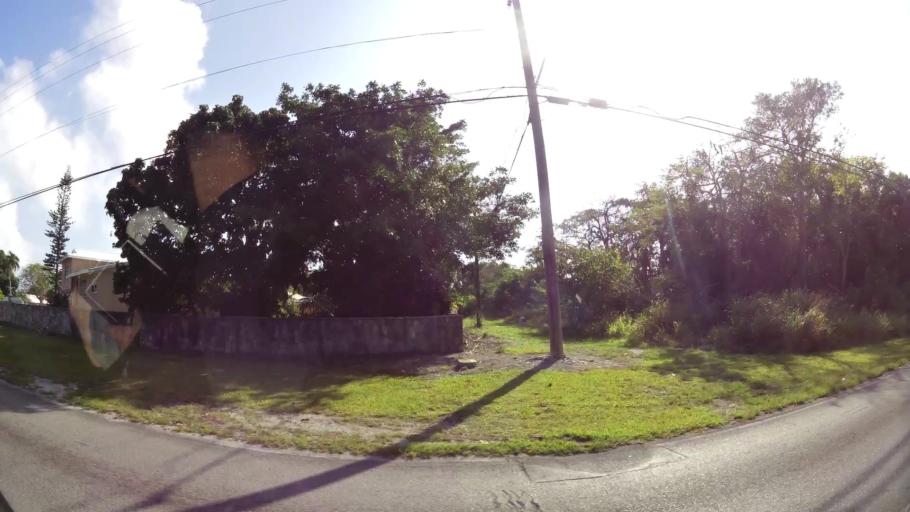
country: BS
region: Freeport
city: Lucaya
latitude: 26.5116
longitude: -78.6613
